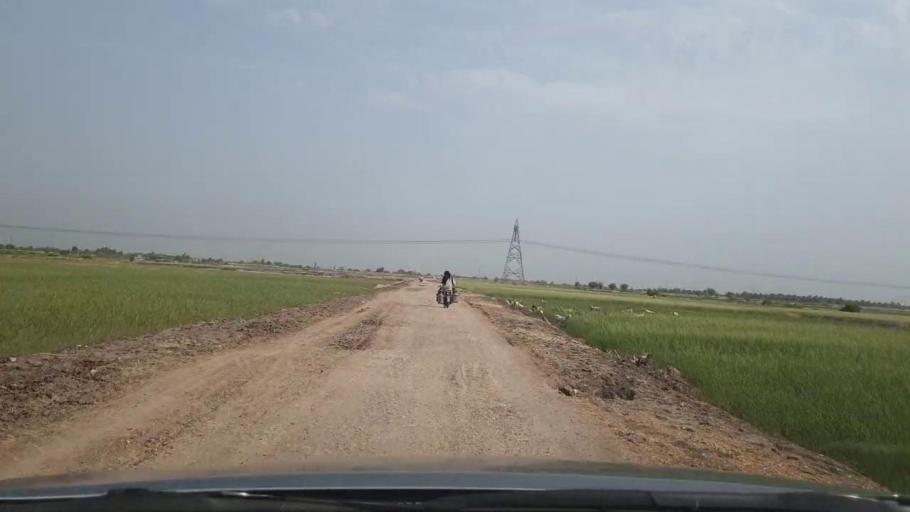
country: PK
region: Sindh
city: Rohri
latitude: 27.6712
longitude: 69.0266
